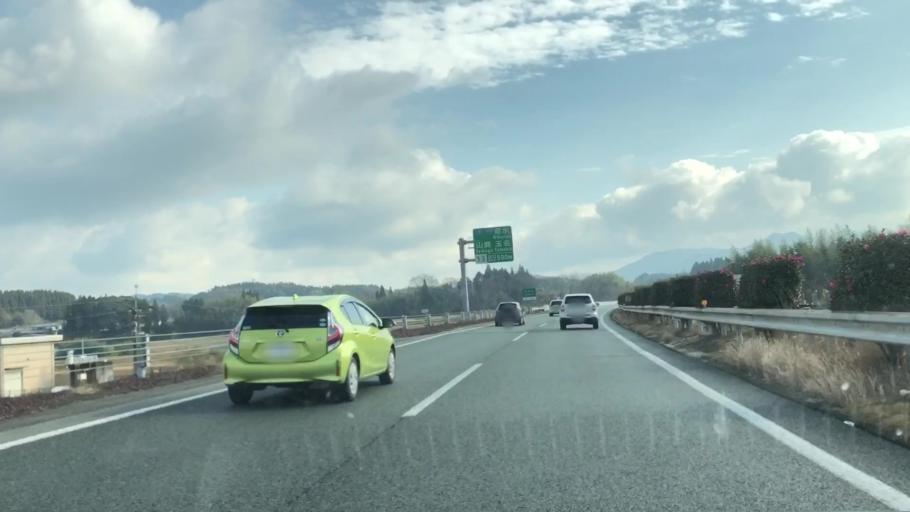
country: JP
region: Kumamoto
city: Tamana
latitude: 32.9937
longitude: 130.6005
